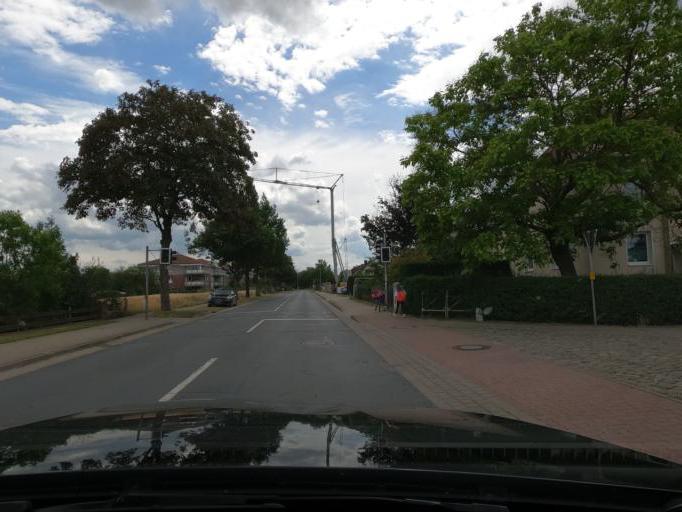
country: DE
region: Lower Saxony
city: Sehnde
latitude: 52.3506
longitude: 9.8979
